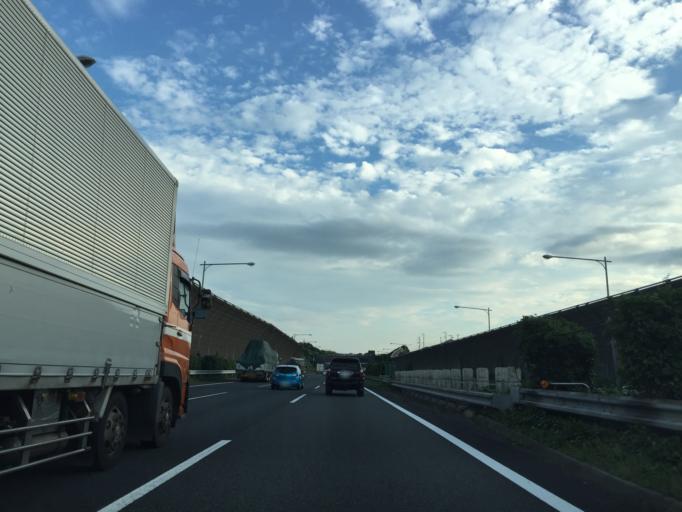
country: JP
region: Kanagawa
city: Hadano
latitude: 35.3743
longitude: 139.2650
